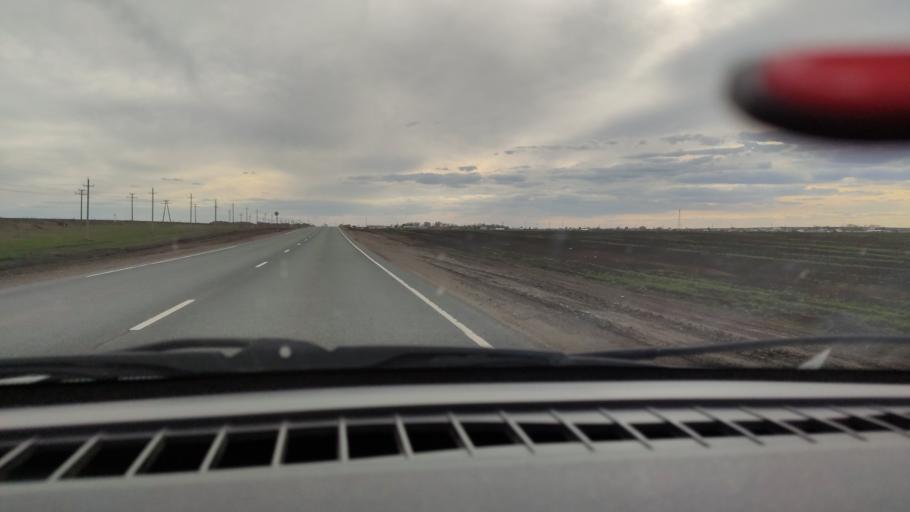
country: RU
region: Bashkortostan
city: Mayachnyy
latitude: 52.3622
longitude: 55.5945
